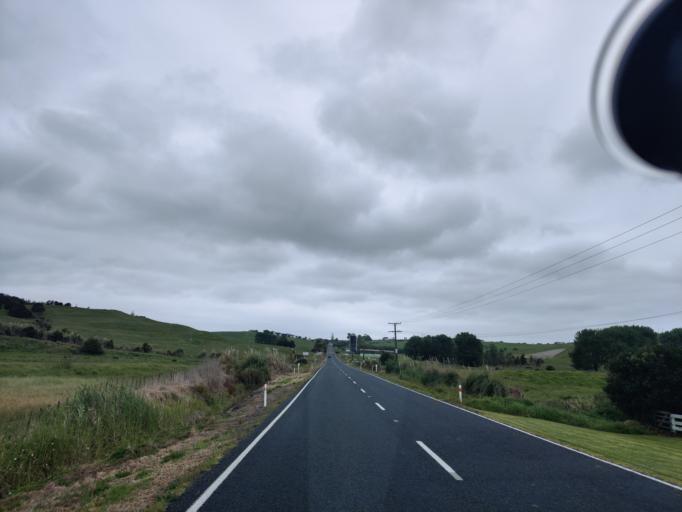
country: NZ
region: Northland
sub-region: Kaipara District
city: Dargaville
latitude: -36.1213
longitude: 174.1071
